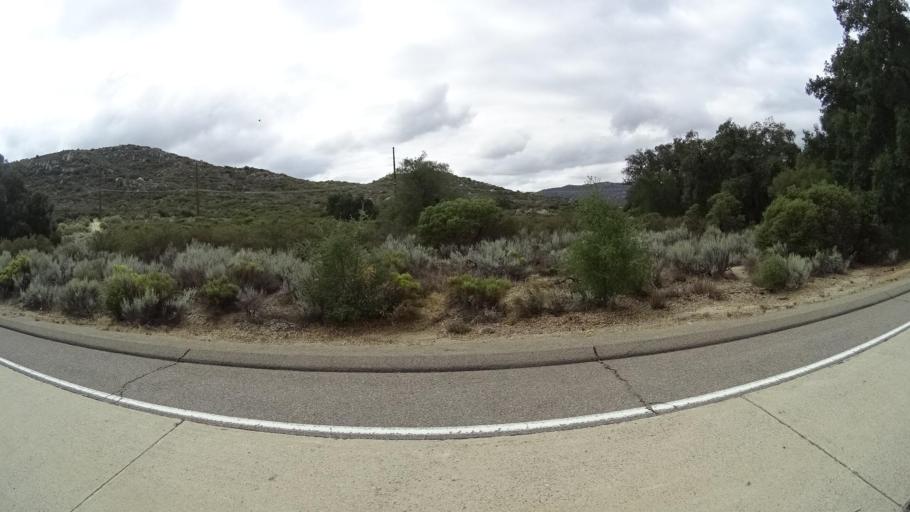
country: US
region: California
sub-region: San Diego County
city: Pine Valley
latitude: 32.7281
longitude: -116.4811
